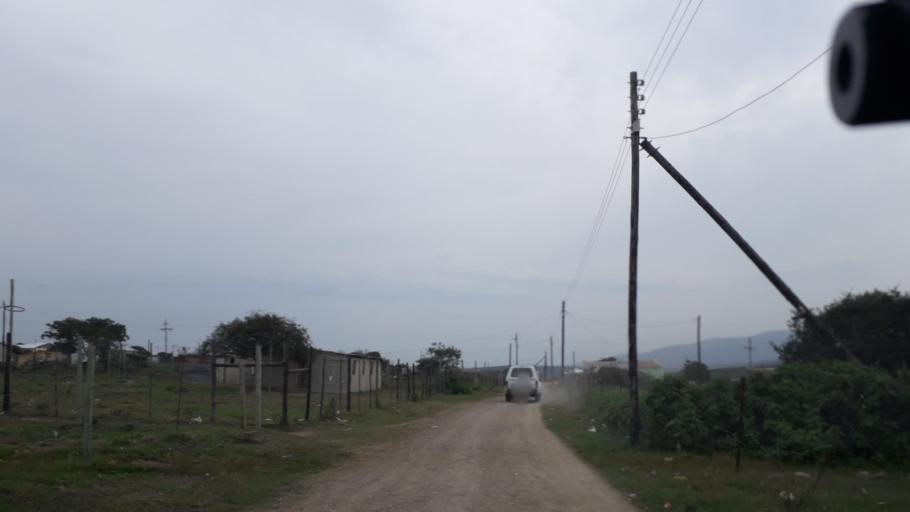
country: ZA
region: Eastern Cape
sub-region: Buffalo City Metropolitan Municipality
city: Bhisho
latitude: -32.8356
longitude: 27.3707
